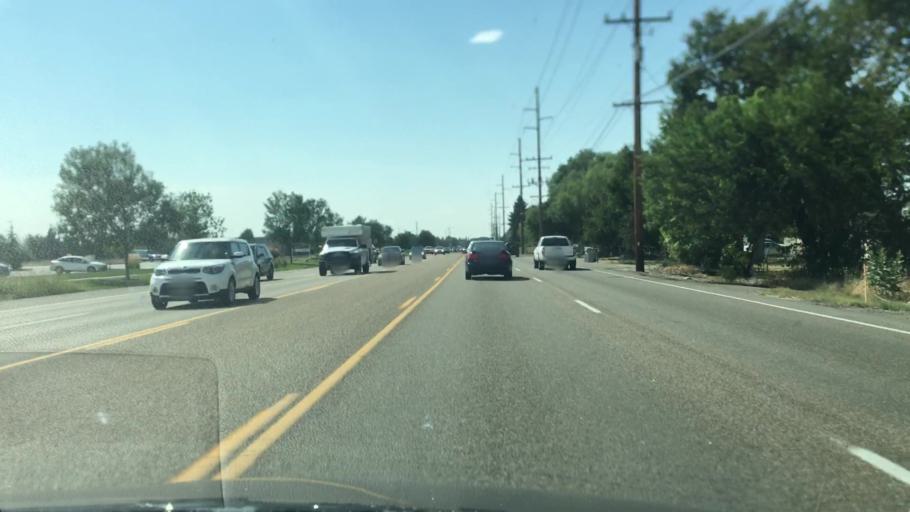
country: US
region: Idaho
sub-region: Ada County
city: Eagle
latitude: 43.6807
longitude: -116.3084
